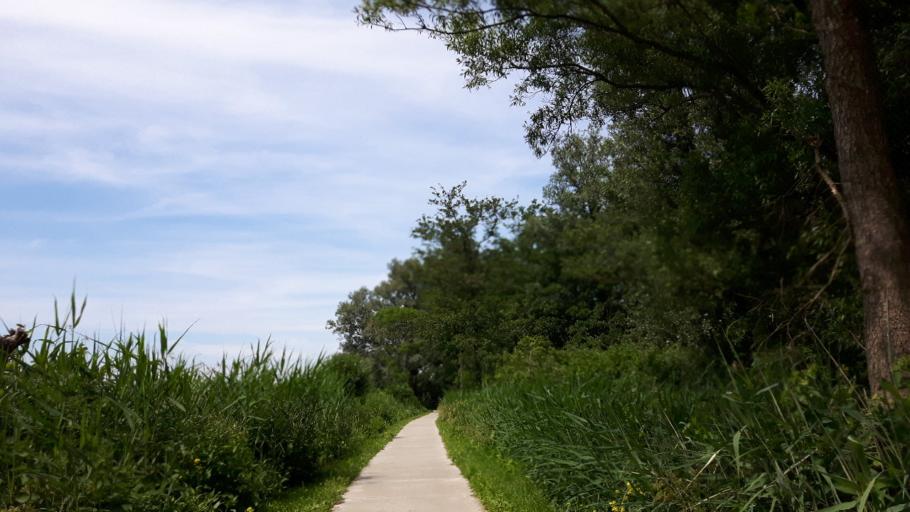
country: NL
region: South Holland
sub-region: Gemeente Nieuwkoop
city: Nieuwkoop
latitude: 52.1316
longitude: 4.7726
